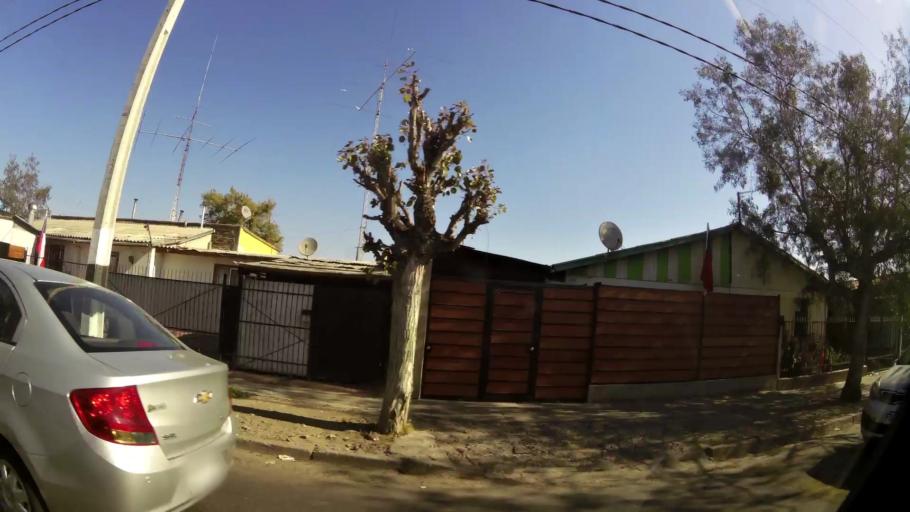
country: CL
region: Santiago Metropolitan
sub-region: Provincia de Santiago
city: Santiago
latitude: -33.5083
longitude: -70.6865
